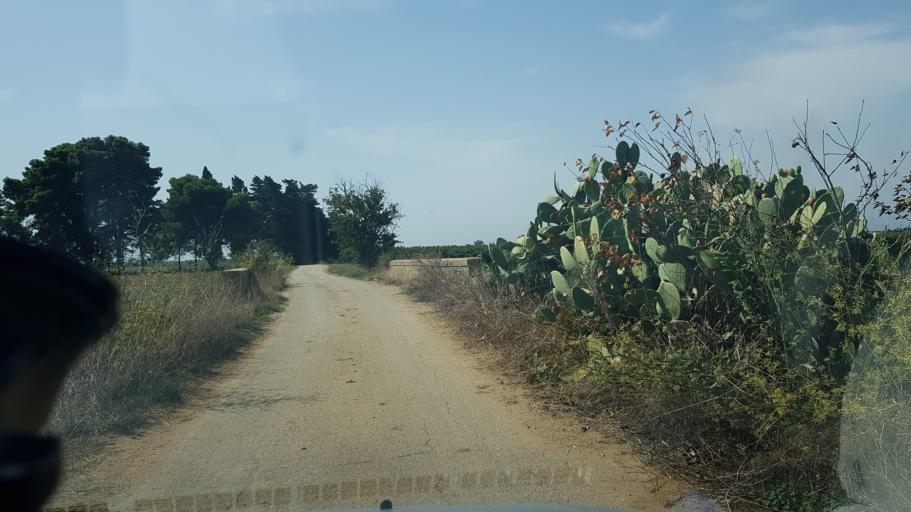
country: IT
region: Apulia
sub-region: Provincia di Brindisi
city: Brindisi
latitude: 40.6001
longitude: 17.8851
